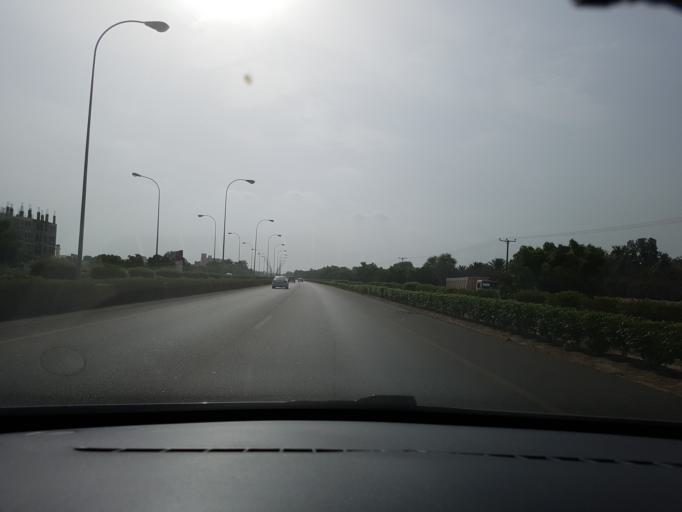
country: OM
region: Al Batinah
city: Al Sohar
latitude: 24.3955
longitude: 56.6762
